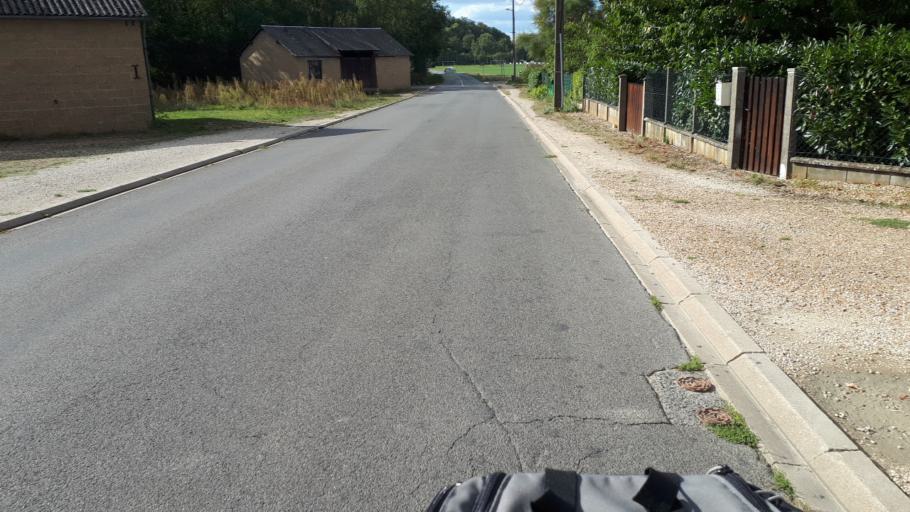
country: FR
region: Centre
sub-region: Departement du Loir-et-Cher
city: Villiers-sur-Loir
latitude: 47.7924
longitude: 0.9607
